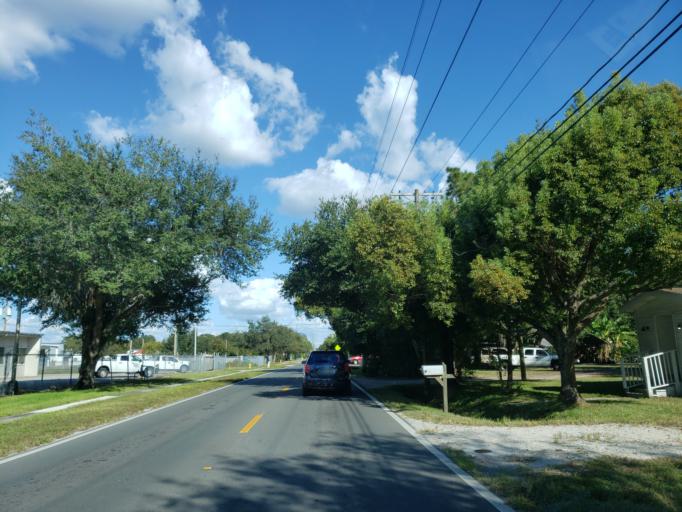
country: US
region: Florida
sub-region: Hillsborough County
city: Plant City
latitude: 28.0037
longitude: -82.1366
